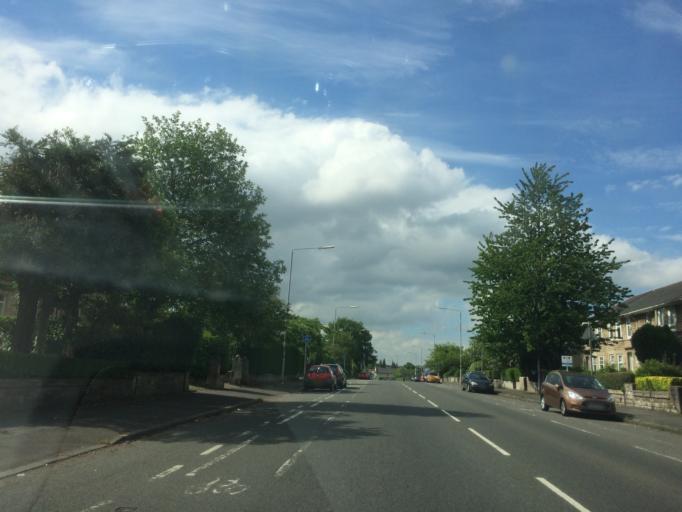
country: GB
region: Scotland
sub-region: East Renfrewshire
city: Giffnock
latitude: 55.8153
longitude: -4.2895
